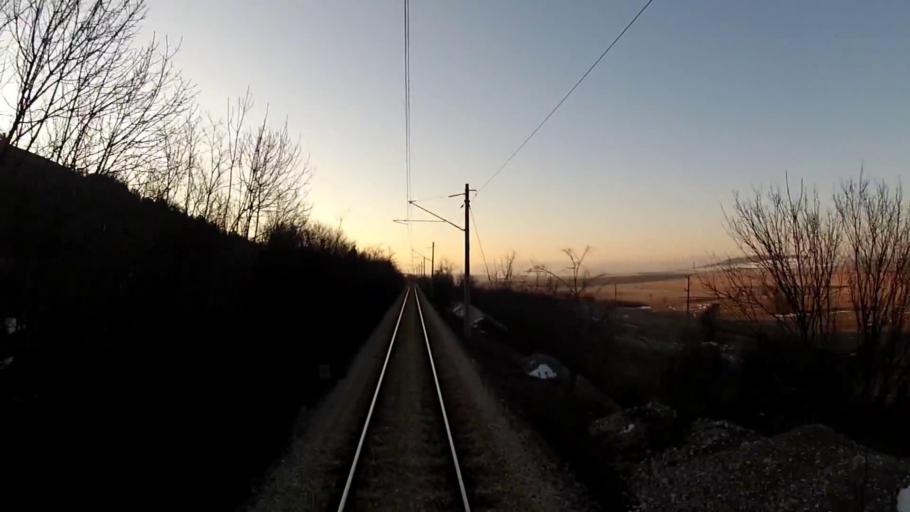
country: BG
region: Sofiya
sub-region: Obshtina Dragoman
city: Dragoman
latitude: 42.9012
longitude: 22.9500
